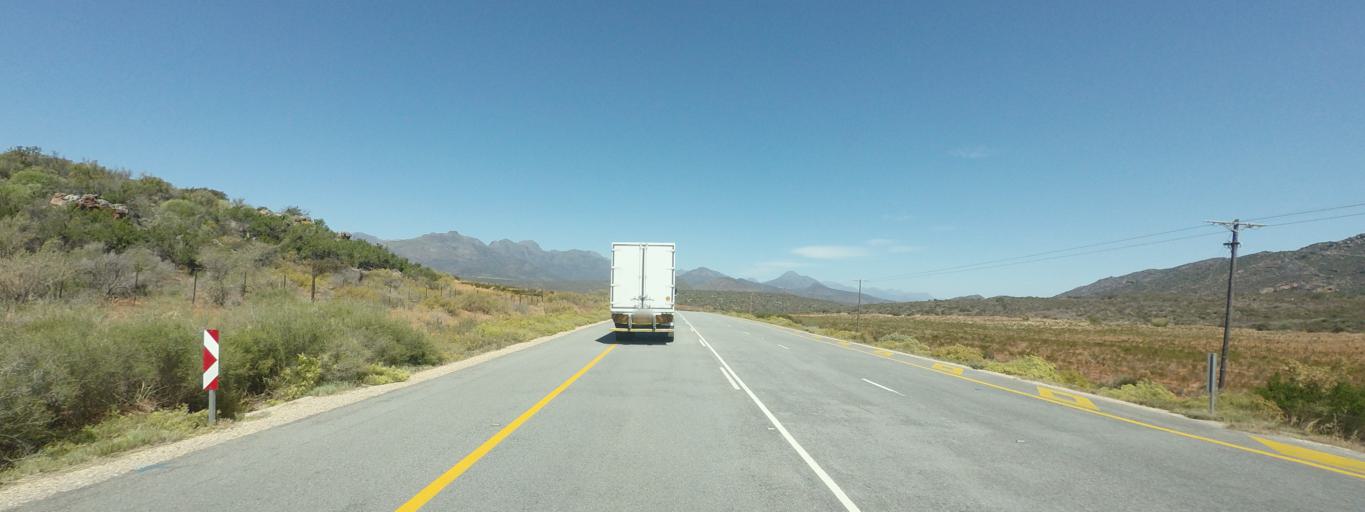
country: ZA
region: Western Cape
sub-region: West Coast District Municipality
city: Clanwilliam
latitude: -32.3232
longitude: 18.9177
